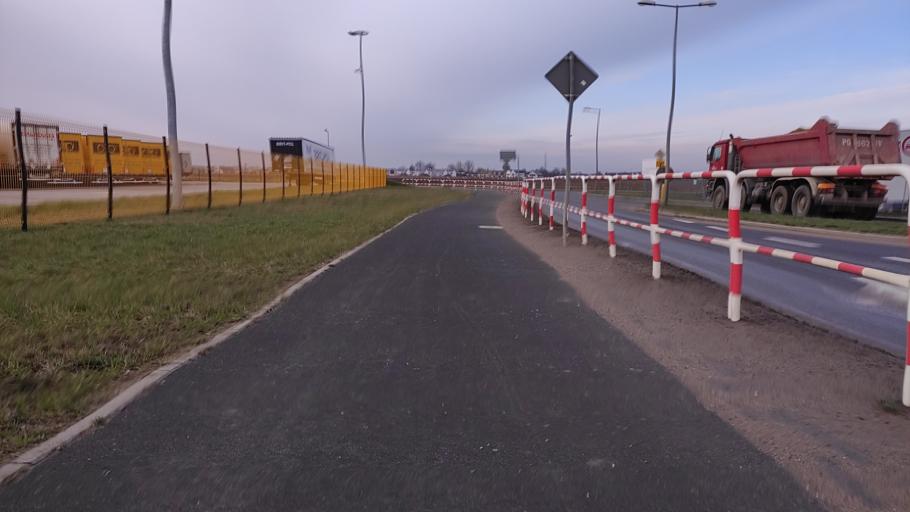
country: PL
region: Greater Poland Voivodeship
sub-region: Powiat poznanski
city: Swarzedz
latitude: 52.3981
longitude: 17.1214
